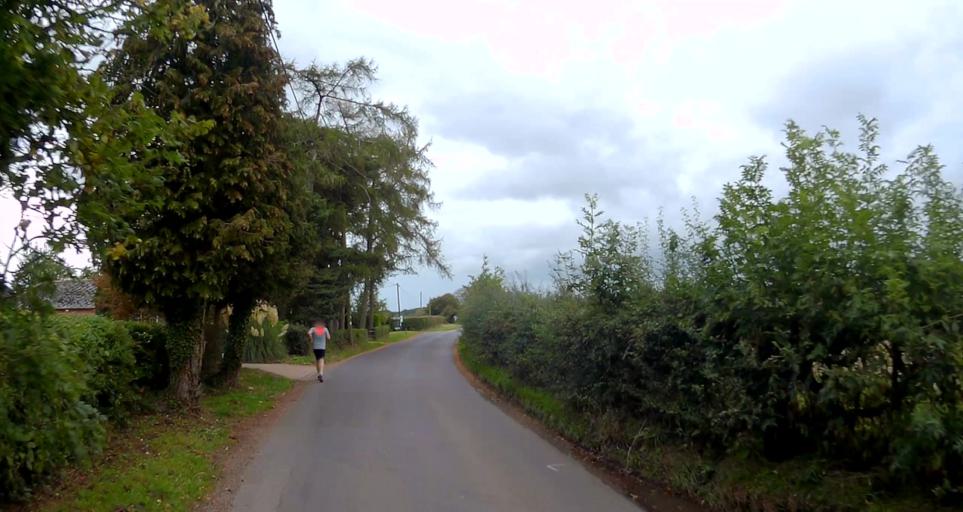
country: GB
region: England
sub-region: Hampshire
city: Four Marks
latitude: 51.1329
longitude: -1.0749
